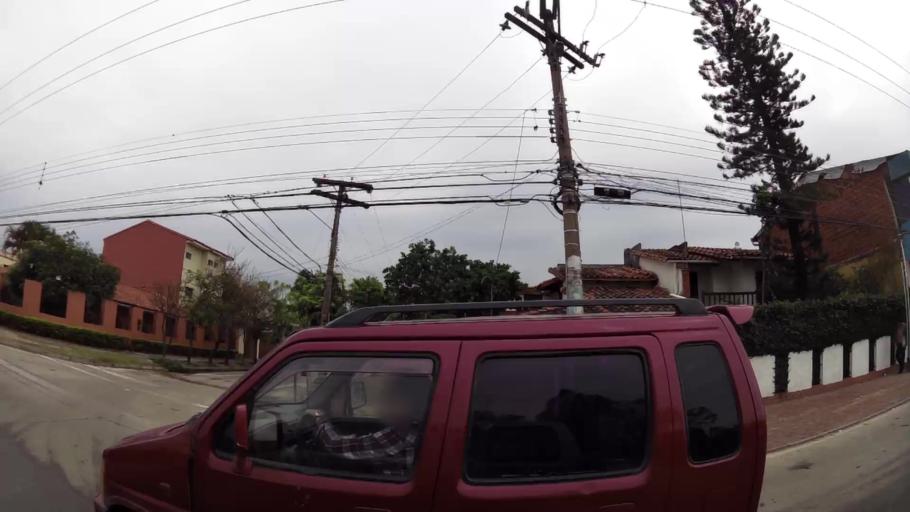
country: BO
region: Santa Cruz
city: Santa Cruz de la Sierra
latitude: -17.7662
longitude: -63.1595
